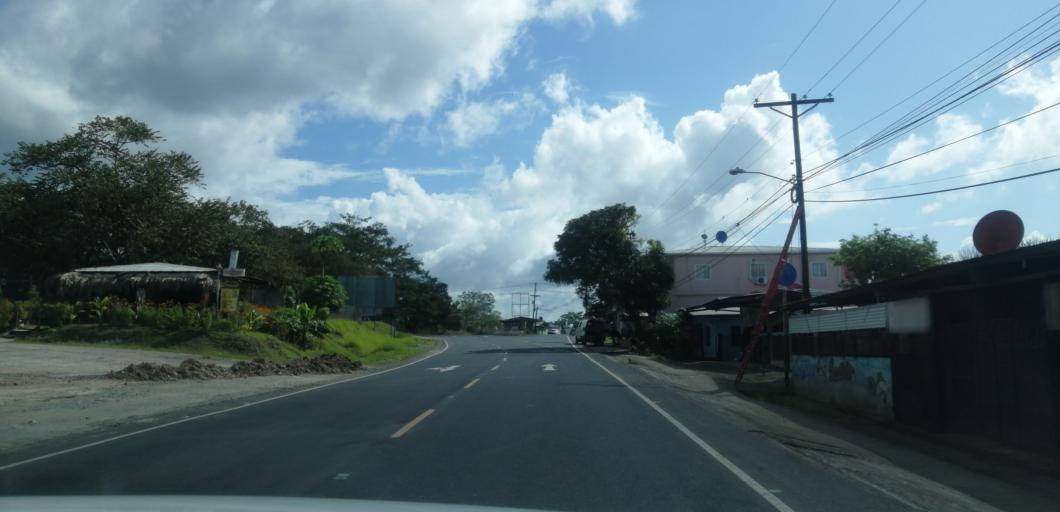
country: PA
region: Panama
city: Canita
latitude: 9.2213
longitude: -78.8924
